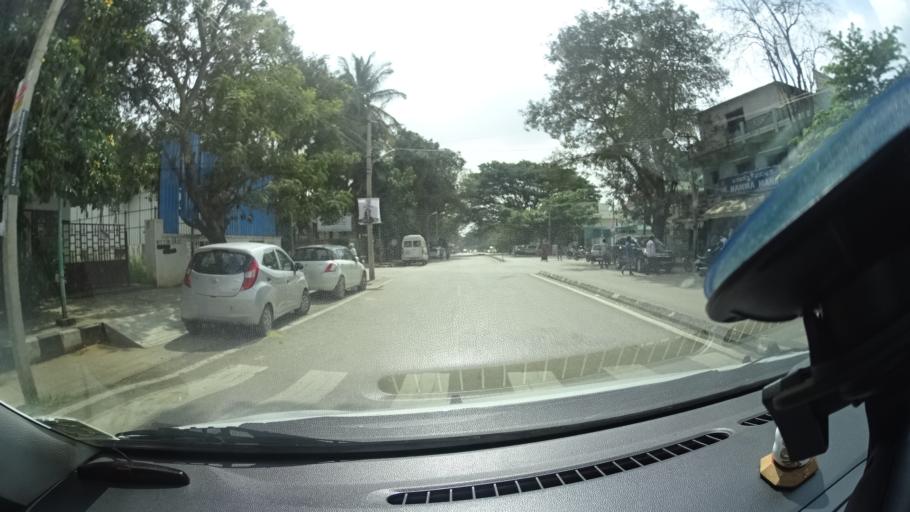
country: IN
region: Karnataka
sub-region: Bangalore Urban
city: Yelahanka
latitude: 13.0968
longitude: 77.5885
